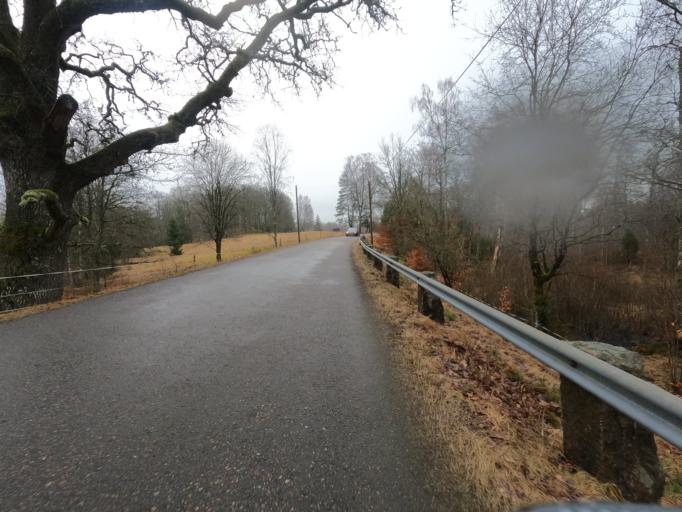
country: SE
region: Halland
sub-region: Hylte Kommun
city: Hyltebruk
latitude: 56.8430
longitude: 13.4715
